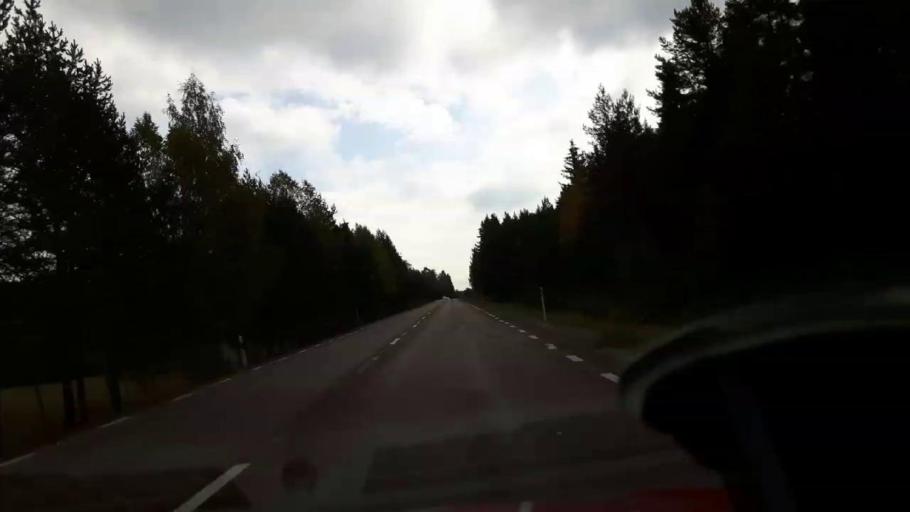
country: SE
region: Gaevleborg
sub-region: Bollnas Kommun
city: Kilafors
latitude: 61.2666
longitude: 16.5457
